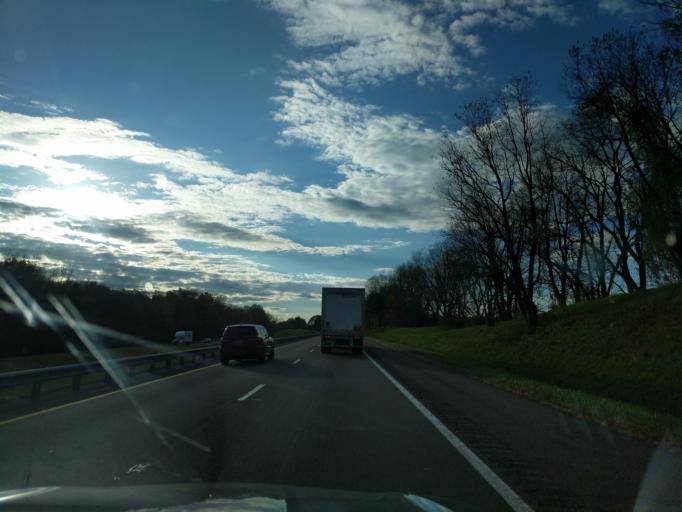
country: US
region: Virginia
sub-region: Washington County
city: Emory
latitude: 36.7696
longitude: -81.8064
